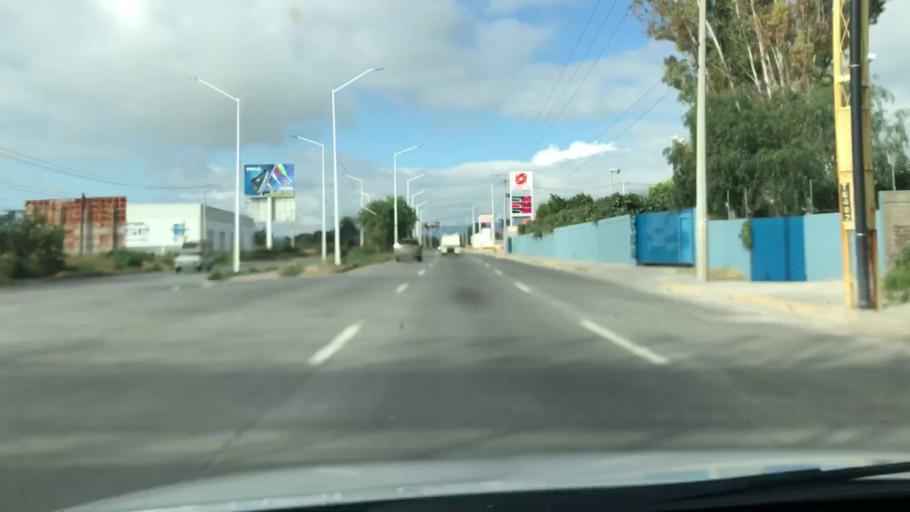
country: MX
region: Guanajuato
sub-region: San Francisco del Rincon
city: Estacion de San Francisco
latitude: 21.0465
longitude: -101.7908
